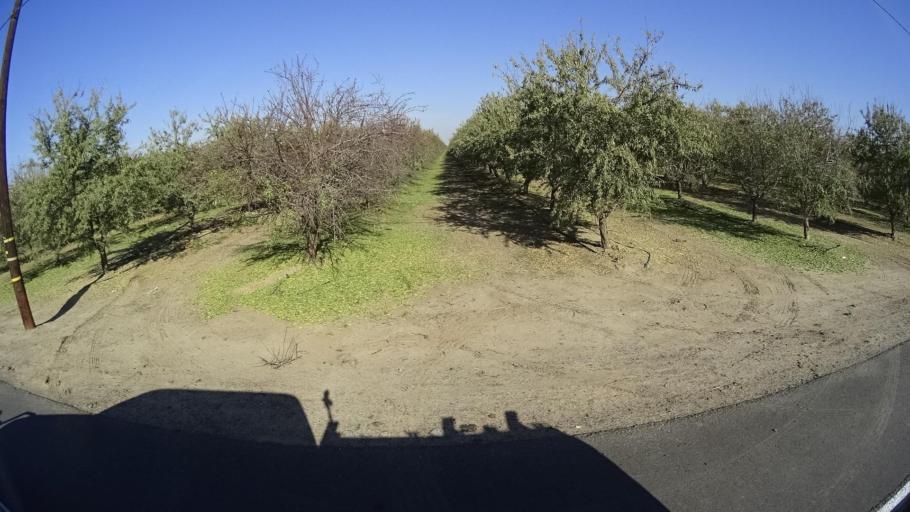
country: US
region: California
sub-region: Kern County
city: Delano
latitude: 35.7178
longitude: -119.3144
